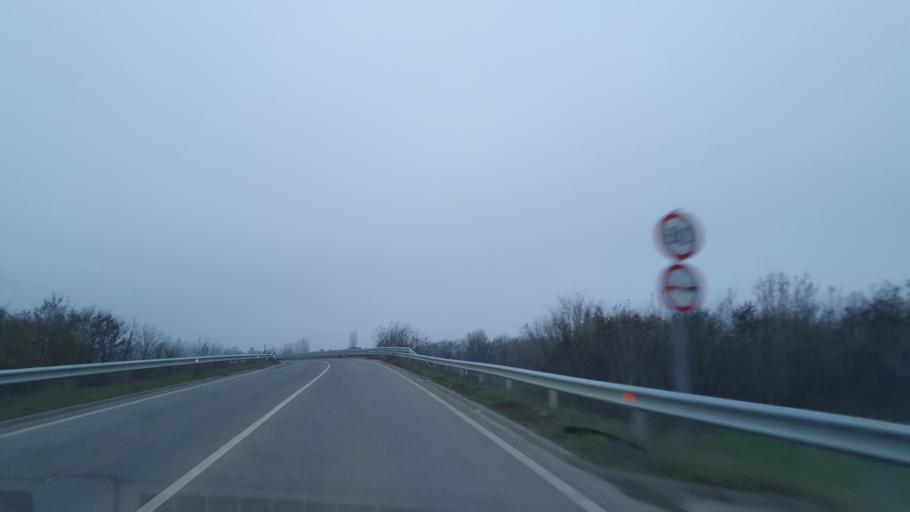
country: HU
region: Pest
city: Csomor
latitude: 47.5362
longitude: 19.2218
